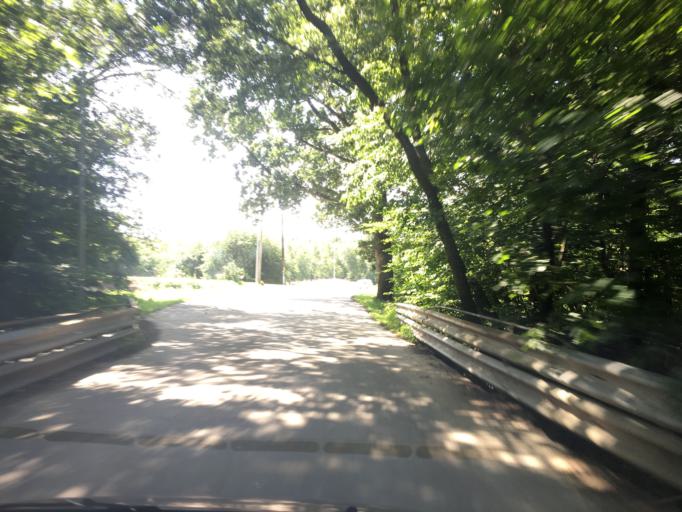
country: SE
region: Skane
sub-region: Svalovs Kommun
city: Kagerod
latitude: 55.9903
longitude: 13.1051
